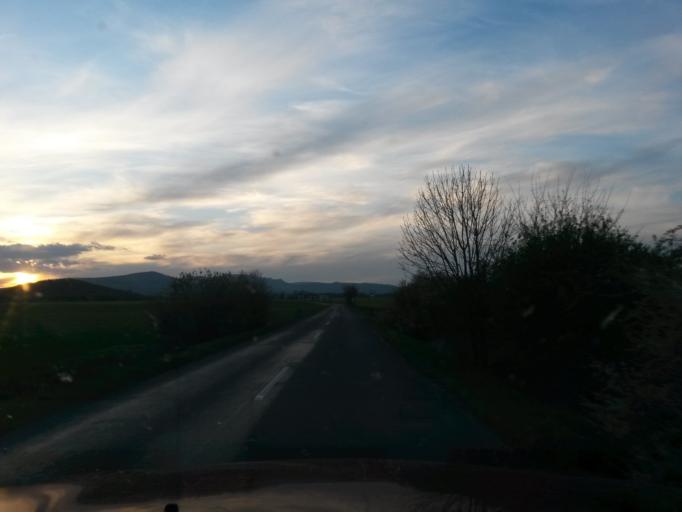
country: HU
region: Borsod-Abauj-Zemplen
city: Satoraljaujhely
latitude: 48.5111
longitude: 21.6107
